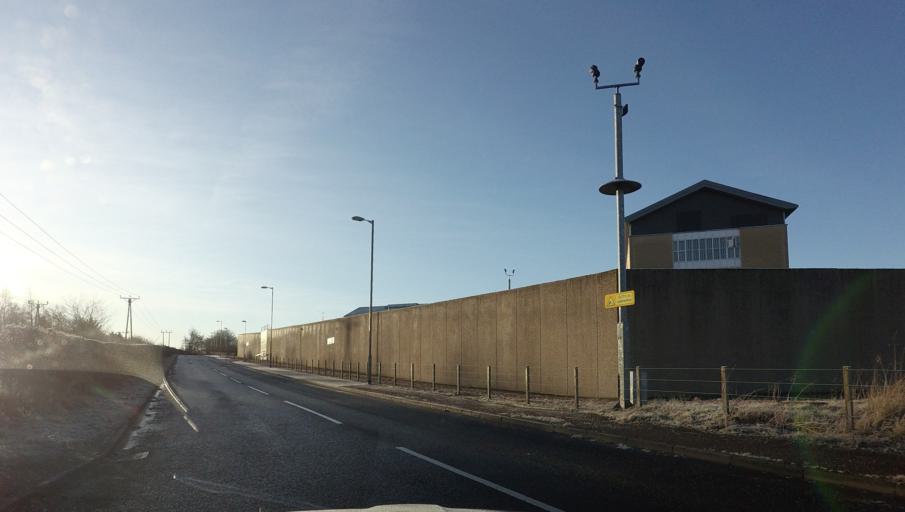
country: GB
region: Scotland
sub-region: North Lanarkshire
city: Shotts
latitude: 55.8300
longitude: -3.8237
